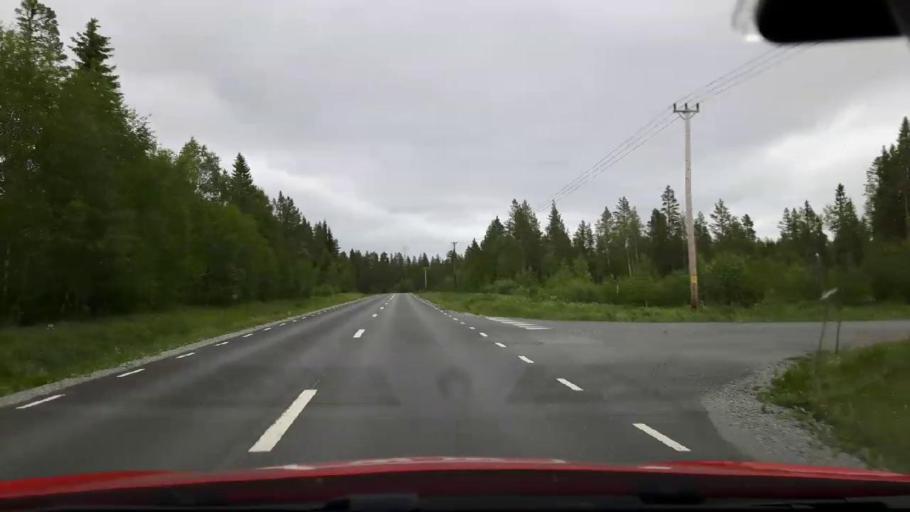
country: SE
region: Jaemtland
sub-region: OEstersunds Kommun
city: Lit
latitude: 63.7380
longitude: 14.7721
